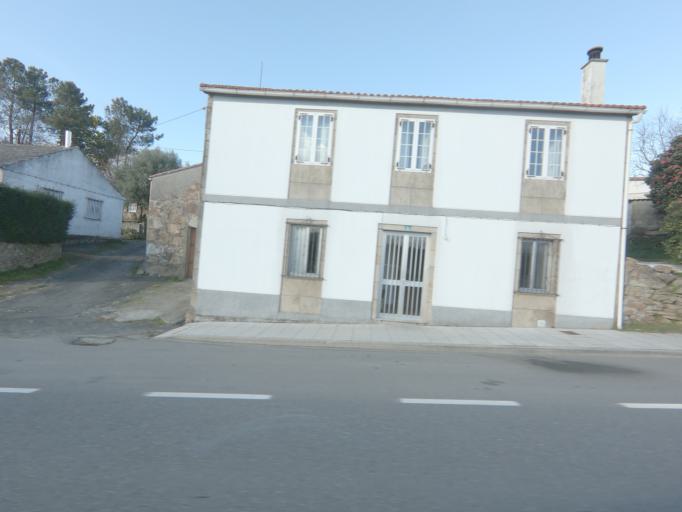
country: ES
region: Galicia
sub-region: Provincia de Pontevedra
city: Silleda
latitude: 42.6993
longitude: -8.2524
